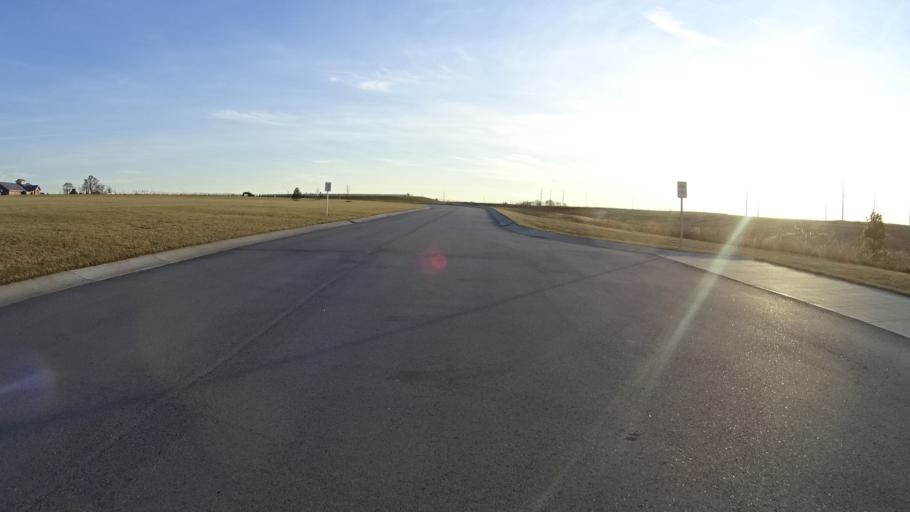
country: US
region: Nebraska
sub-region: Sarpy County
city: Chalco
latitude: 41.1368
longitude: -96.1340
